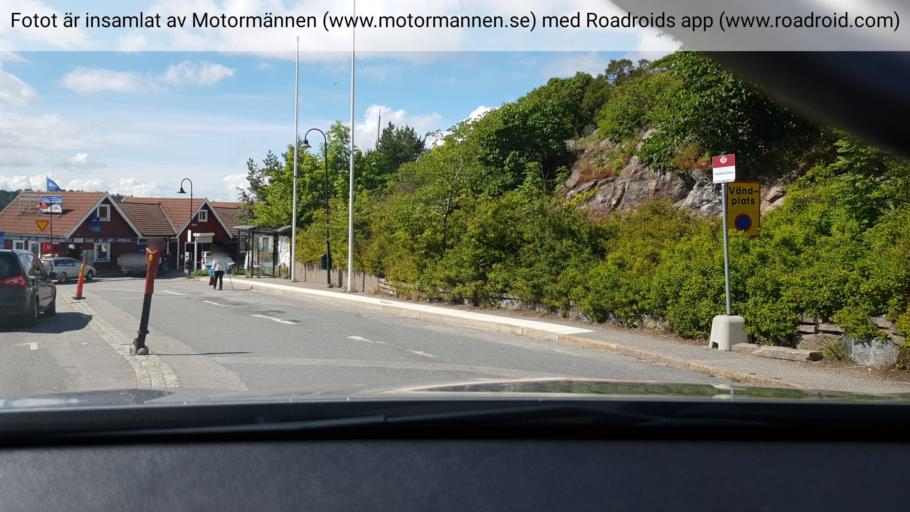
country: SE
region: Stockholm
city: Dalaro
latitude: 59.1301
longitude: 18.4052
